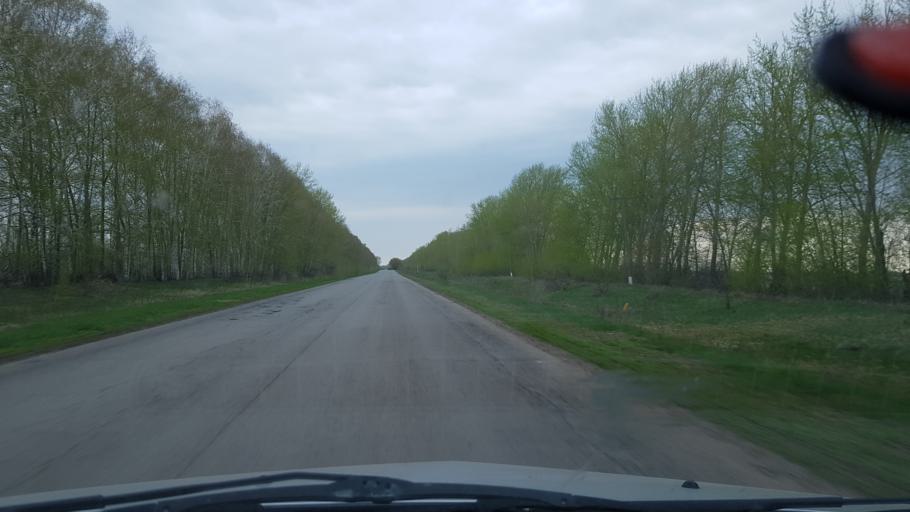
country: RU
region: Samara
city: Podstepki
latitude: 53.6640
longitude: 49.1850
